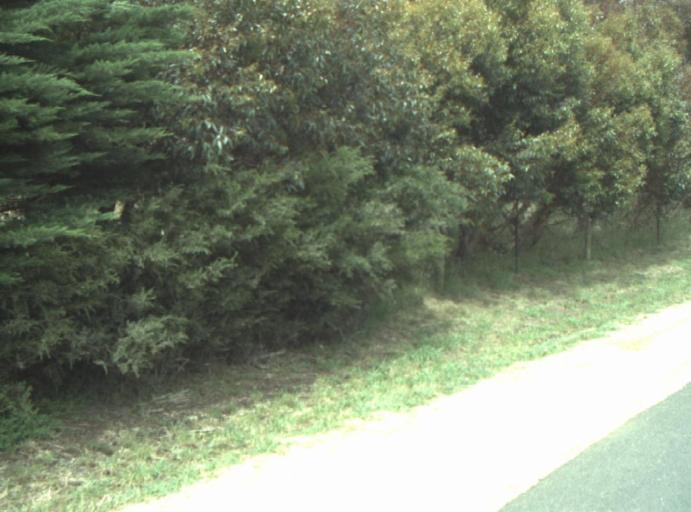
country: AU
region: Victoria
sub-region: Greater Geelong
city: Wandana Heights
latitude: -38.2299
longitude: 144.2800
